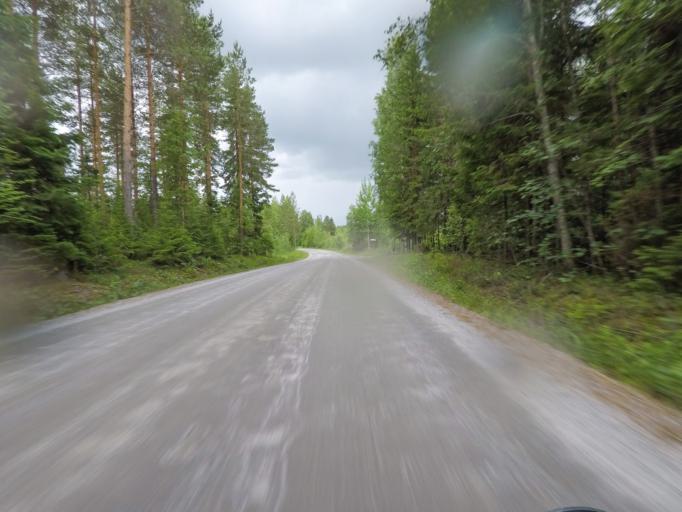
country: FI
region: Central Finland
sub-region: Jyvaeskylae
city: Hankasalmi
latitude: 62.4033
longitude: 26.6026
